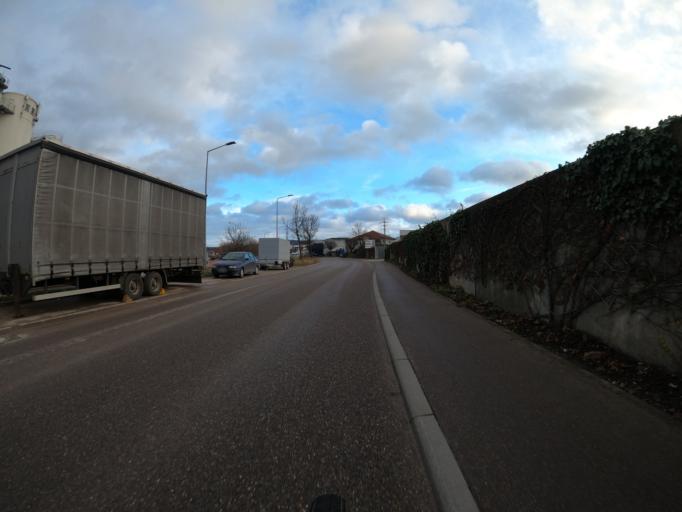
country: DE
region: Baden-Wuerttemberg
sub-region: Regierungsbezirk Stuttgart
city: Salach
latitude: 48.6856
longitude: 9.7293
